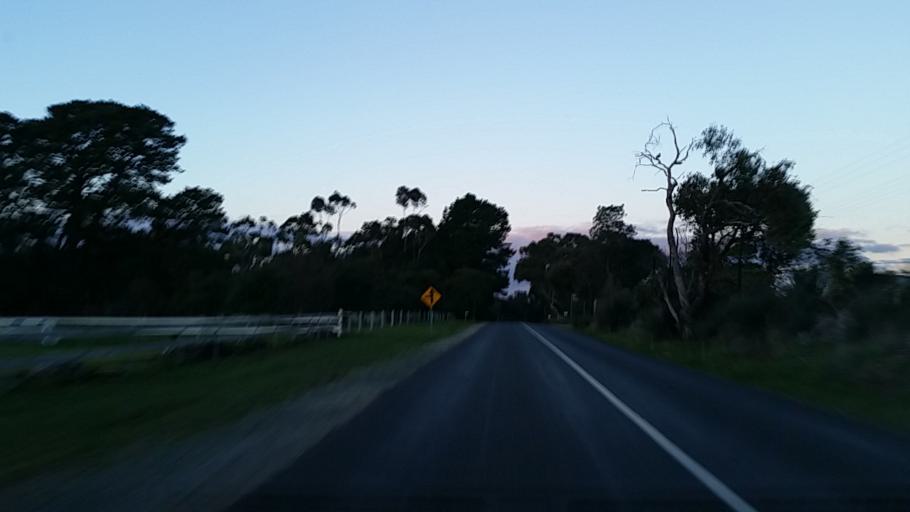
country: AU
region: South Australia
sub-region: Alexandrina
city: Mount Compass
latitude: -35.3175
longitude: 138.6319
